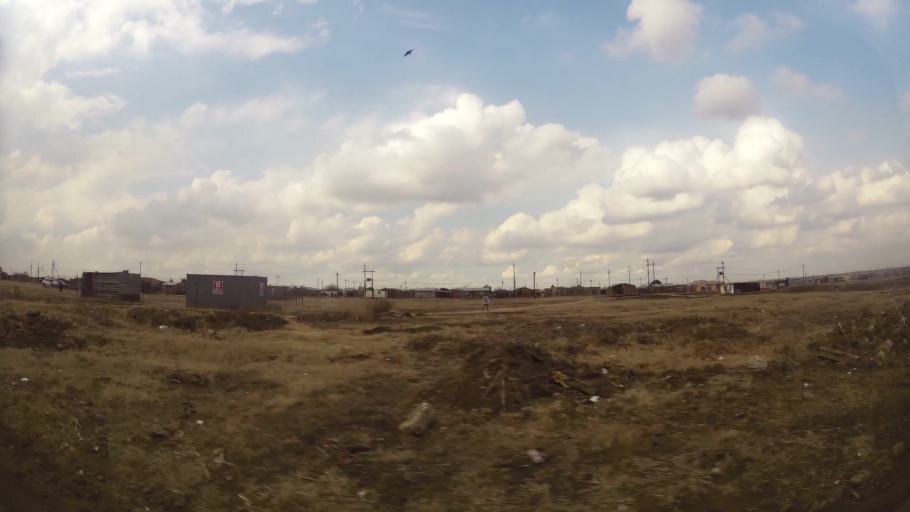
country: ZA
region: Orange Free State
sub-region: Fezile Dabi District Municipality
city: Sasolburg
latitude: -26.8606
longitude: 27.8949
